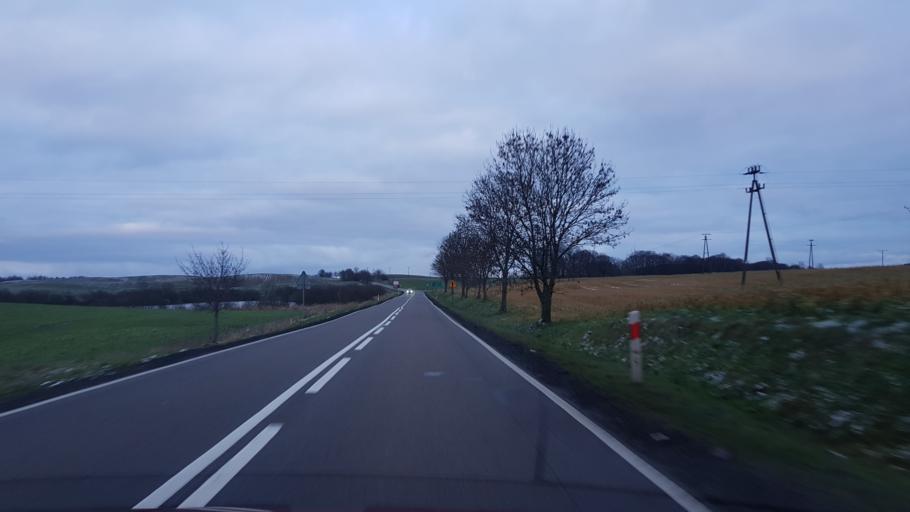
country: PL
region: Pomeranian Voivodeship
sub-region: Powiat czluchowski
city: Koczala
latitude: 54.0257
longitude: 17.1801
